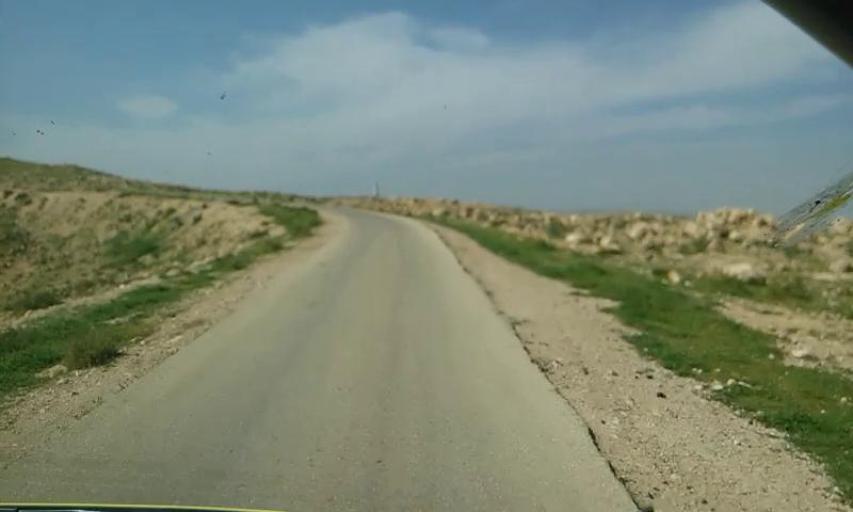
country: PS
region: West Bank
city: Khallat al Mayyah
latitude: 31.4410
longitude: 35.2045
